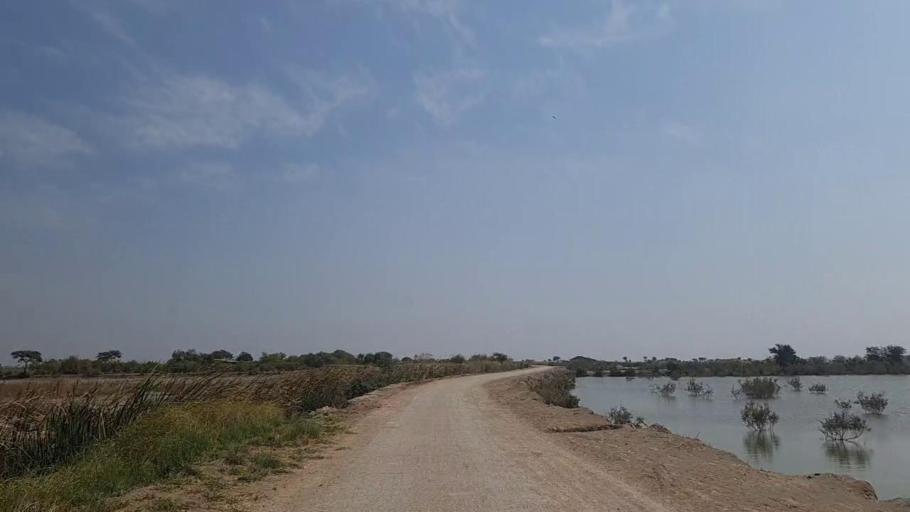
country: PK
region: Sindh
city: Mirpur Batoro
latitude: 24.5856
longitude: 68.2950
